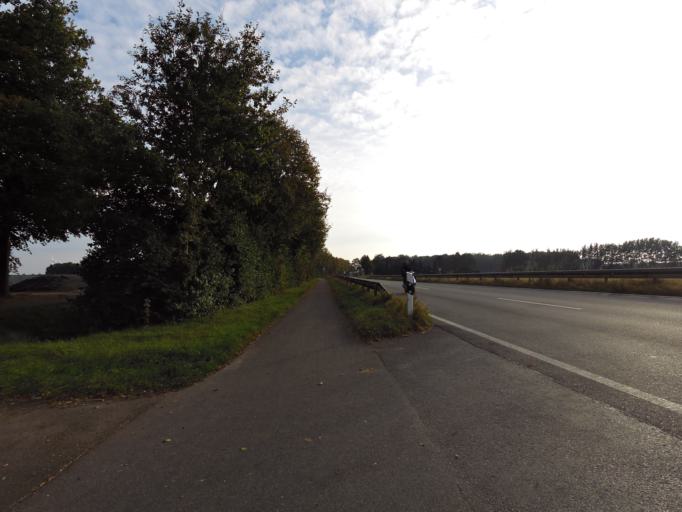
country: DE
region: North Rhine-Westphalia
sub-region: Regierungsbezirk Dusseldorf
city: Bocholt
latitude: 51.8072
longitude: 6.5622
